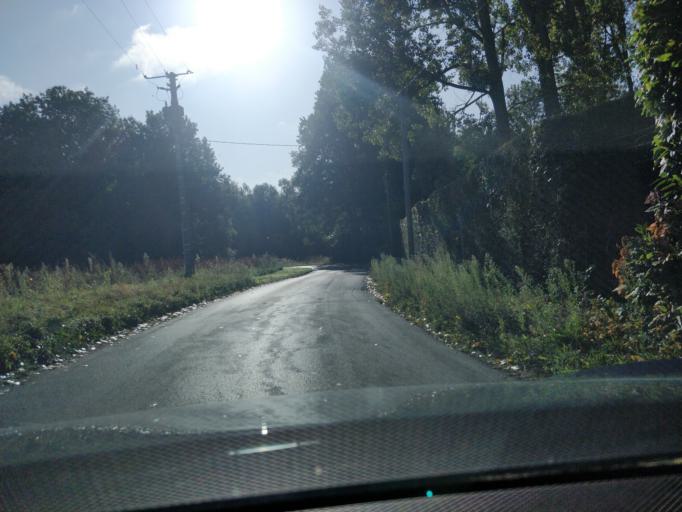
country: FR
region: Ile-de-France
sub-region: Departement de l'Essonne
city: Vaugrigneuse
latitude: 48.6025
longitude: 2.0997
